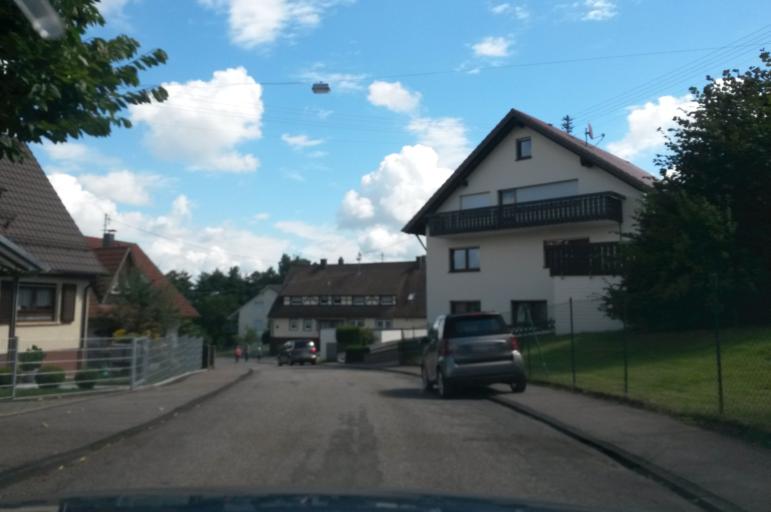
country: DE
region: Baden-Wuerttemberg
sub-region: Karlsruhe Region
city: Dobel
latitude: 48.8422
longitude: 8.4991
